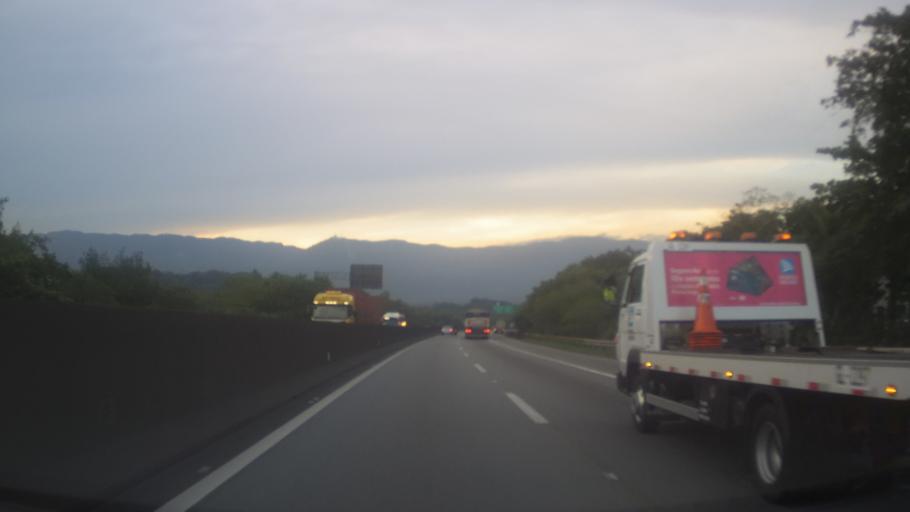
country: BR
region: Sao Paulo
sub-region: Cubatao
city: Cubatao
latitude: -23.9118
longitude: -46.4232
